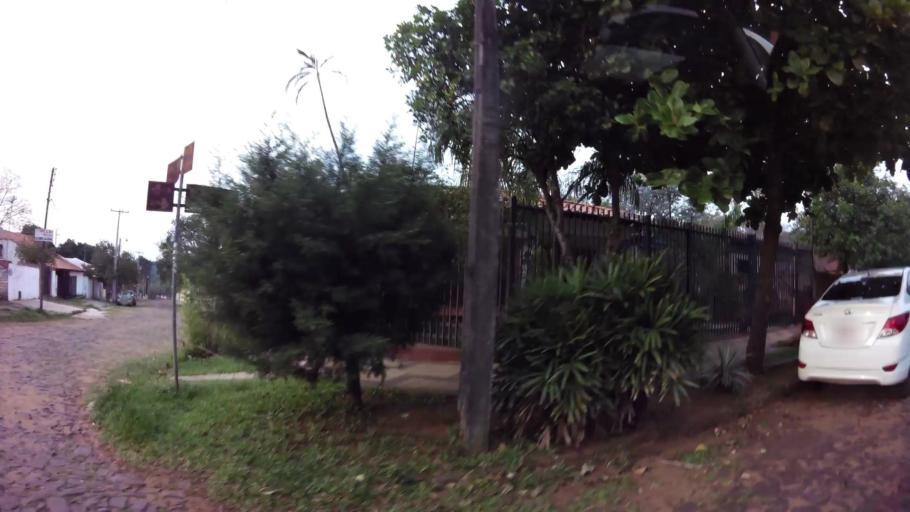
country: PY
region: Central
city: Lambare
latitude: -25.3394
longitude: -57.5951
